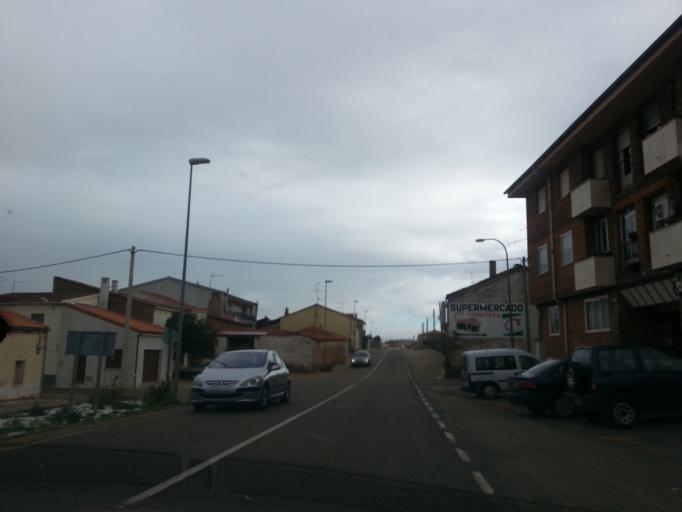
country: ES
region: Castille and Leon
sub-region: Provincia de Salamanca
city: Tamames
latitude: 40.6566
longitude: -6.1047
